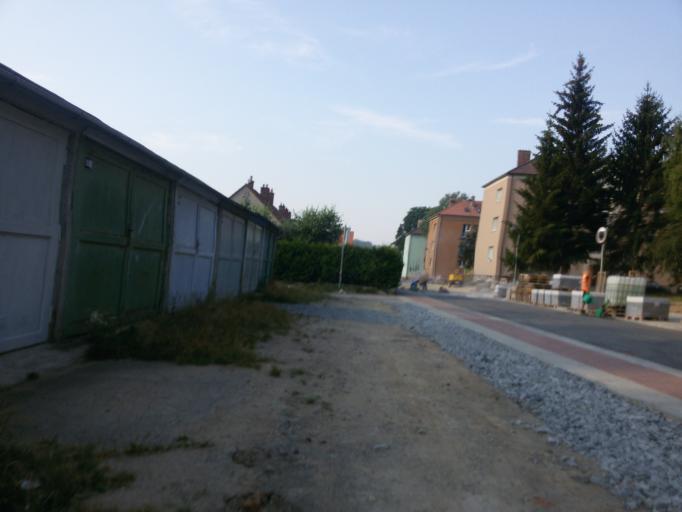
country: CZ
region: South Moravian
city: Kurim
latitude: 49.3076
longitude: 16.5335
